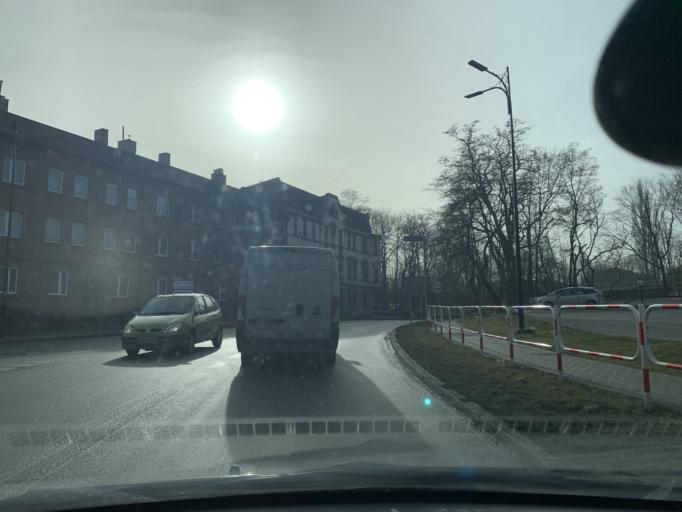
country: PL
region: Silesian Voivodeship
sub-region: Ruda Slaska
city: Ruda Slaska
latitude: 50.3162
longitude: 18.8567
